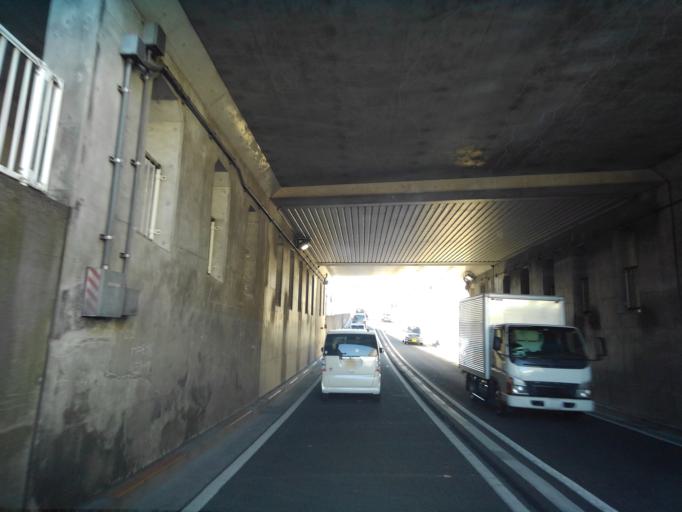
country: JP
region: Tokyo
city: Hino
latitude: 35.7084
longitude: 139.3783
